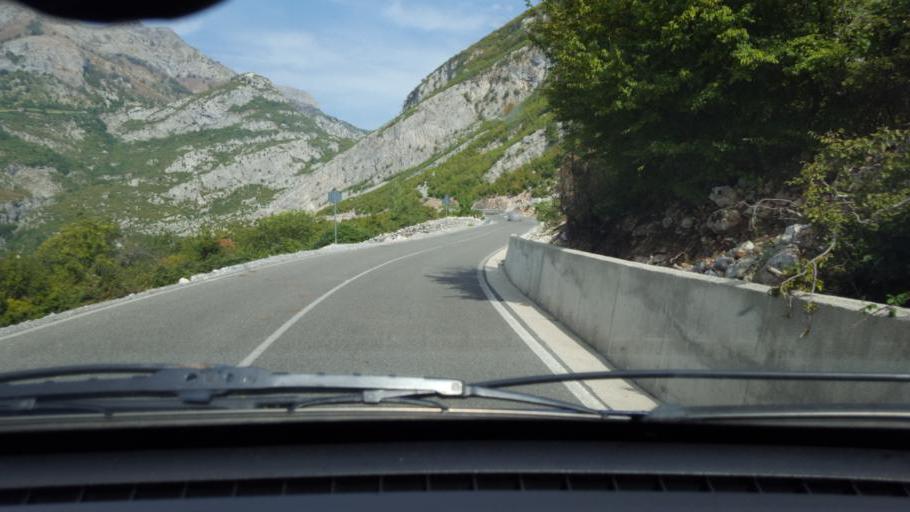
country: AL
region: Shkoder
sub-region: Rrethi i Malesia e Madhe
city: Kastrat
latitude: 42.5146
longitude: 19.6215
